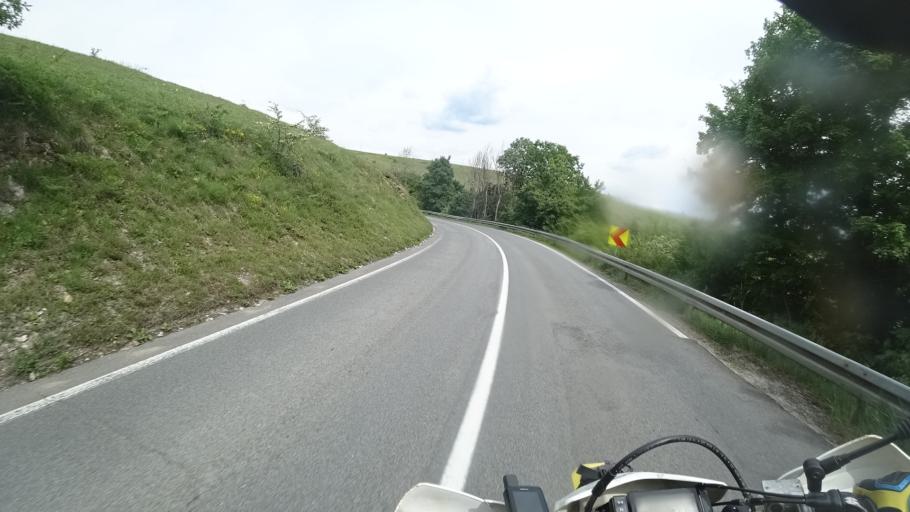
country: BA
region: Federation of Bosnia and Herzegovina
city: Izacic
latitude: 44.9188
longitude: 15.7089
